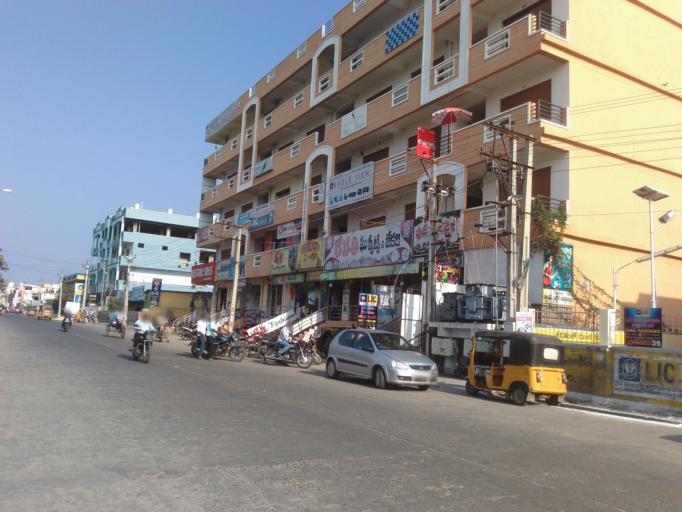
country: IN
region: Andhra Pradesh
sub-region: Prakasam
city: Chirala
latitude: 15.8298
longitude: 80.3522
